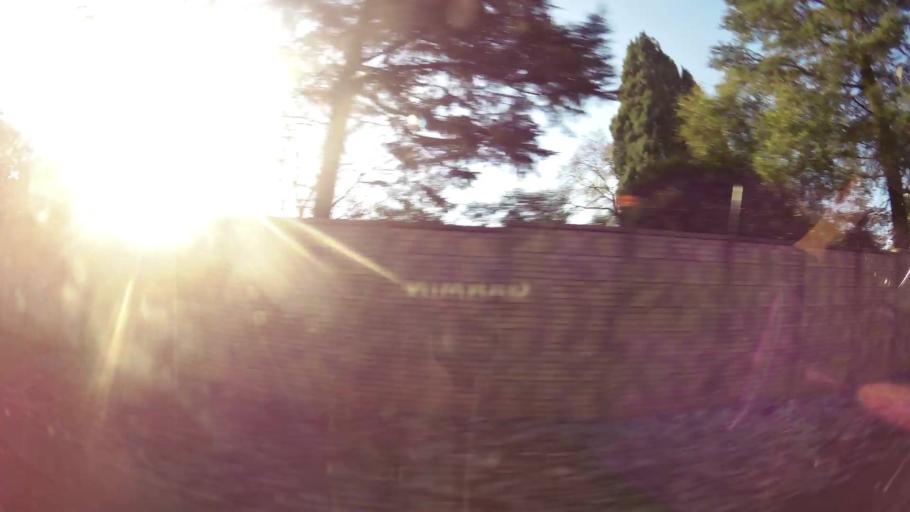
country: ZA
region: Gauteng
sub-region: City of Tshwane Metropolitan Municipality
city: Centurion
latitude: -25.8688
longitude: 28.1443
